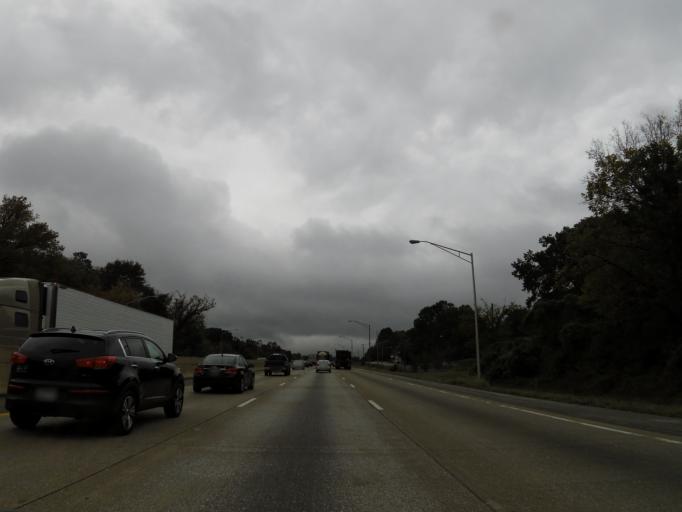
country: US
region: Tennessee
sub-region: Hamilton County
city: East Ridge
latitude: 35.0116
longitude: -85.2453
